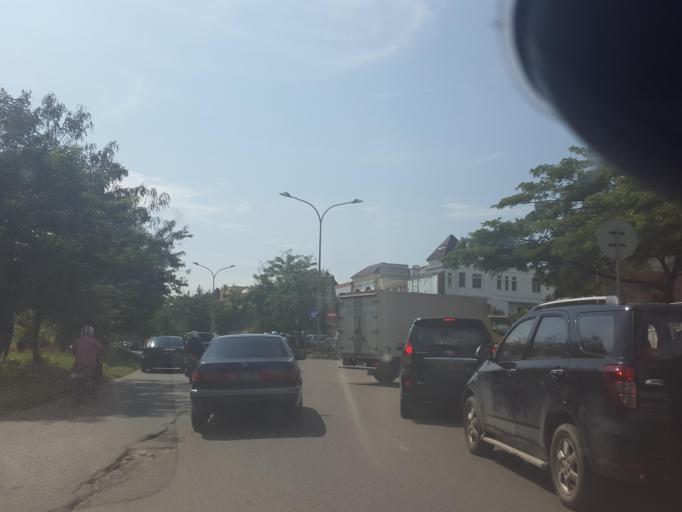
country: SG
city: Singapore
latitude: 1.1367
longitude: 104.0265
